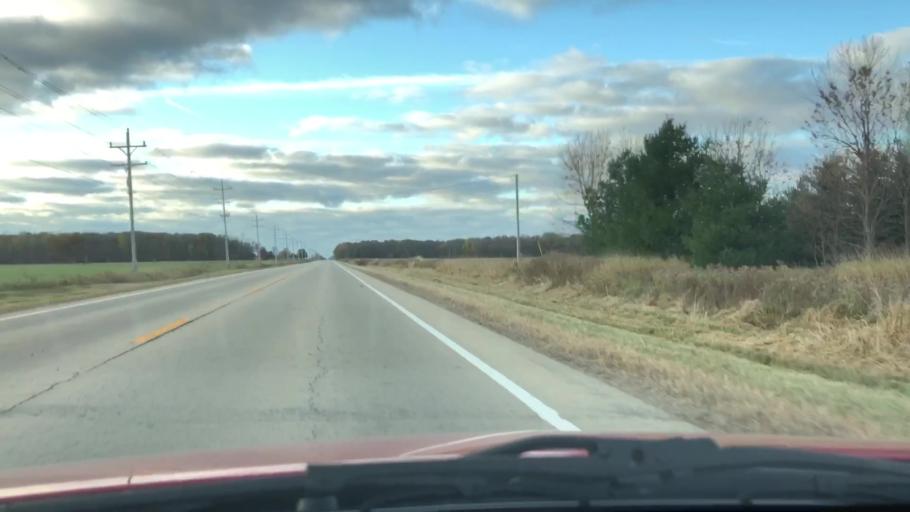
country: US
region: Wisconsin
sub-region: Outagamie County
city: Seymour
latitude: 44.4704
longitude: -88.2911
